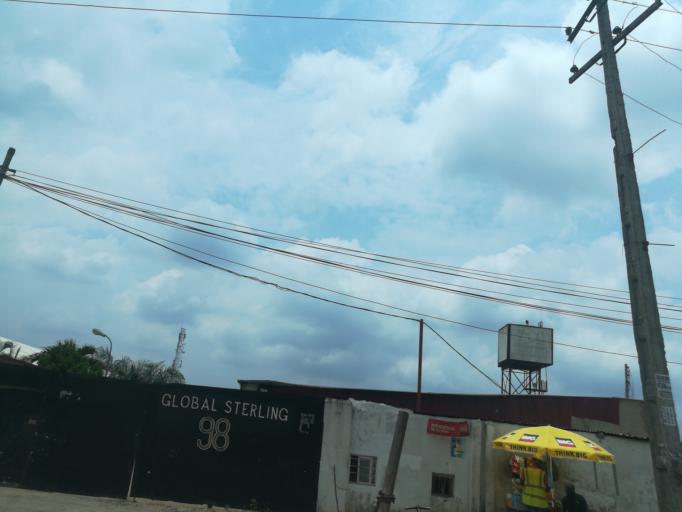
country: NG
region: Lagos
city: Ojota
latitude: 6.5935
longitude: 3.3714
